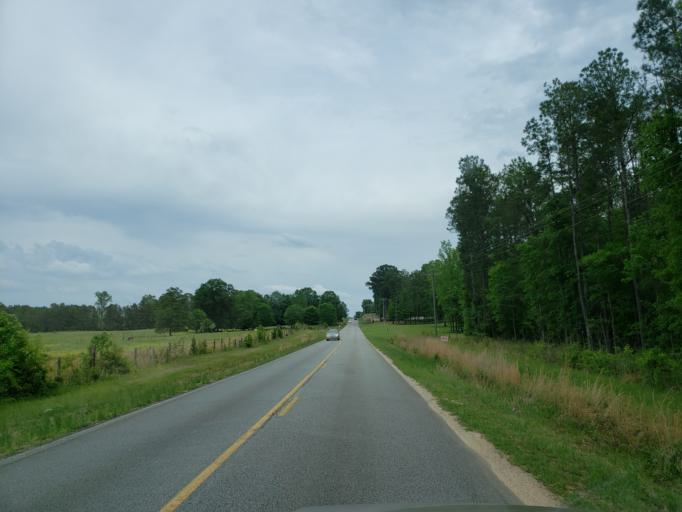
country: US
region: Georgia
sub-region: Bibb County
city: West Point
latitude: 32.8270
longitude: -83.8810
